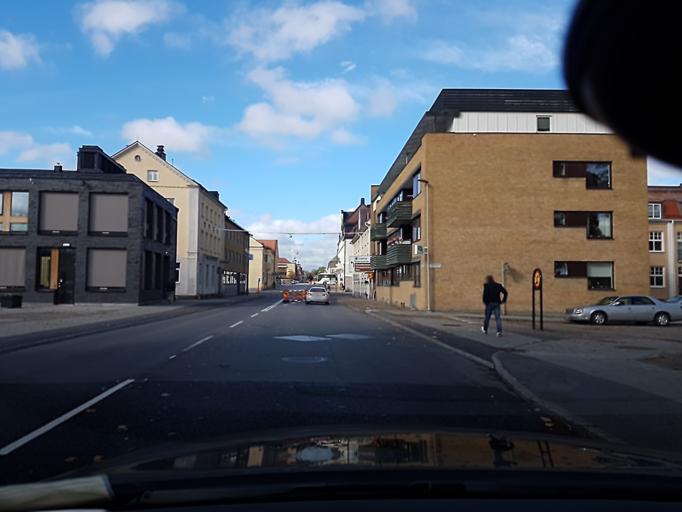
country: SE
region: Kronoberg
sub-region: Vaxjo Kommun
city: Vaexjoe
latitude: 56.8783
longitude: 14.8129
